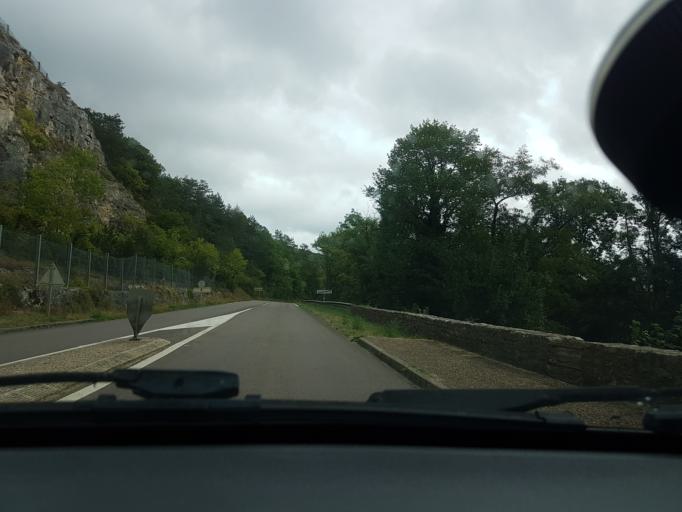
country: FR
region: Bourgogne
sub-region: Departement de l'Yonne
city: Joux-la-Ville
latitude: 47.5785
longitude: 3.7800
